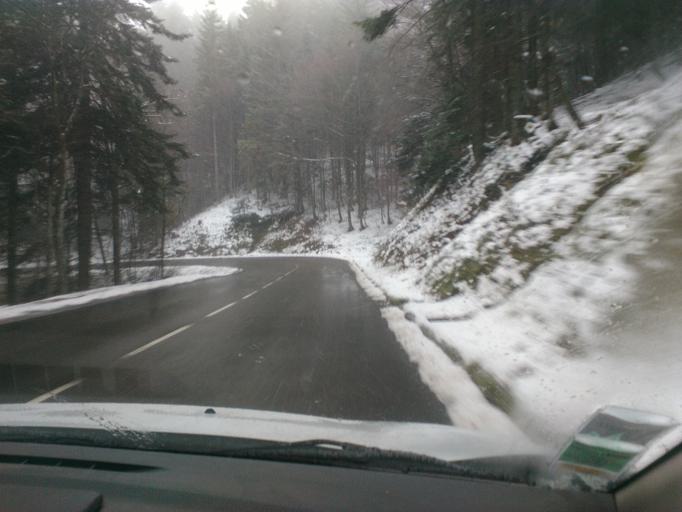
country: FR
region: Lorraine
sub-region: Departement des Vosges
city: Xonrupt-Longemer
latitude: 48.0631
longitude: 6.9953
